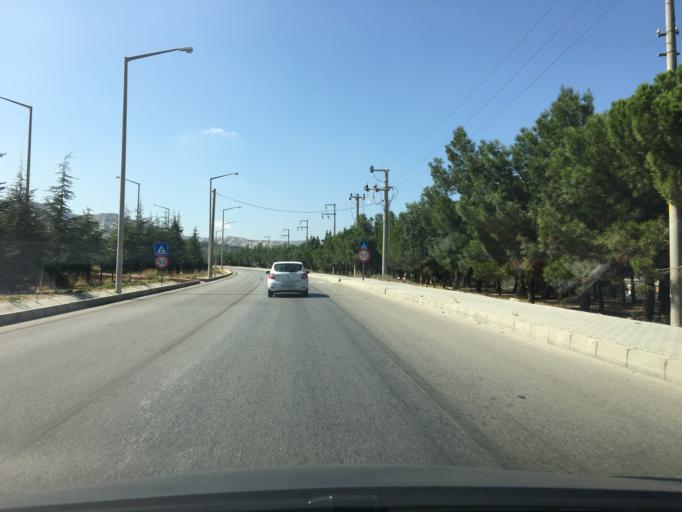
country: TR
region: Burdur
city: Burdur
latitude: 37.7267
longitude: 30.3009
